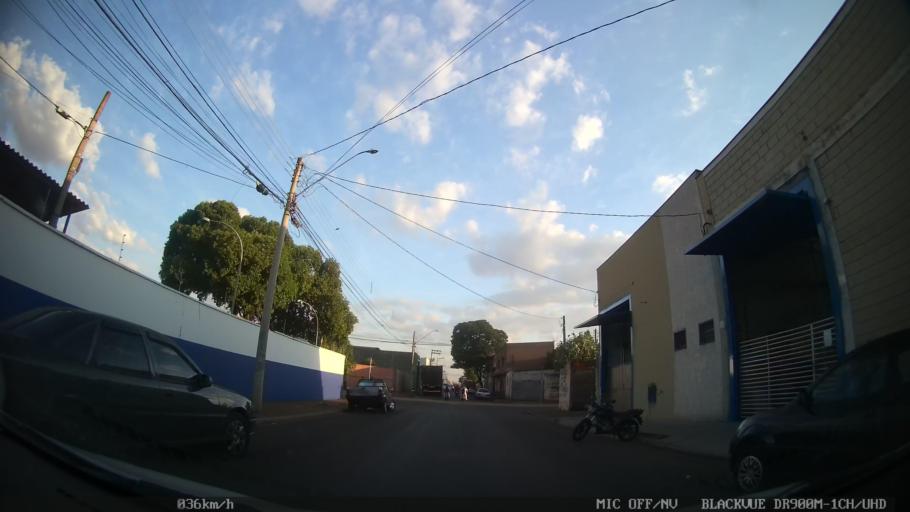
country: BR
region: Sao Paulo
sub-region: Ribeirao Preto
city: Ribeirao Preto
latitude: -21.1412
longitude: -47.7893
